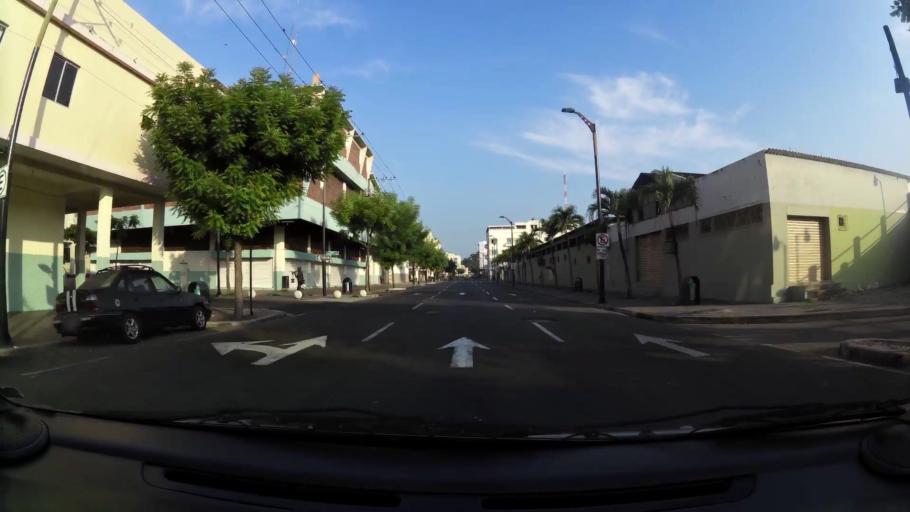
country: EC
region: Guayas
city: Eloy Alfaro
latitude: -2.1854
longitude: -79.8775
